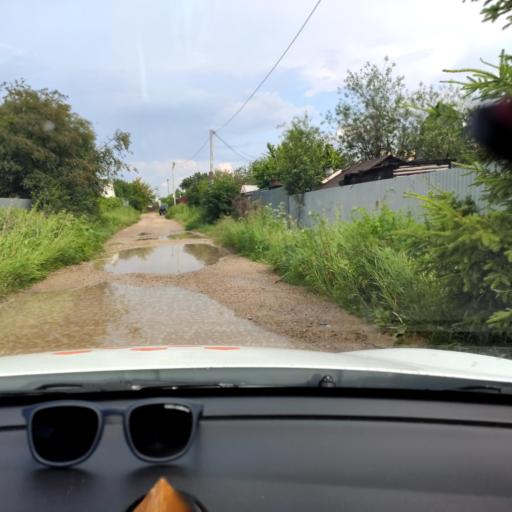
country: RU
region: Tatarstan
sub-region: Zelenodol'skiy Rayon
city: Vasil'yevo
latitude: 55.8225
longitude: 48.7280
